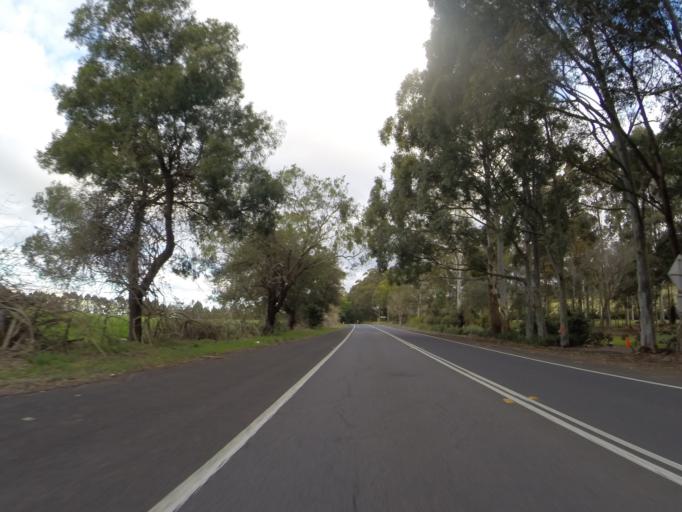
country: AU
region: New South Wales
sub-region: Shellharbour
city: Calderwood
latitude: -34.5773
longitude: 150.6923
